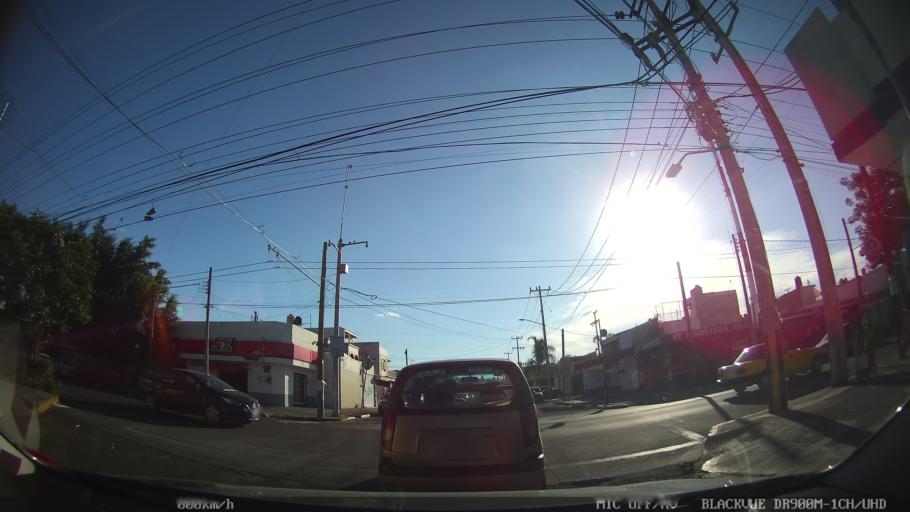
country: MX
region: Jalisco
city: Tlaquepaque
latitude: 20.7006
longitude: -103.2948
